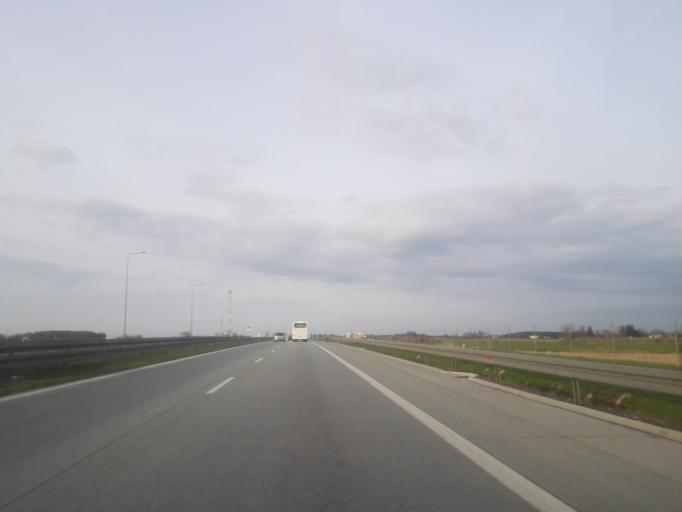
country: PL
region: Lodz Voivodeship
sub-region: Powiat tomaszowski
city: Czerniewice
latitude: 51.6666
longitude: 20.1740
